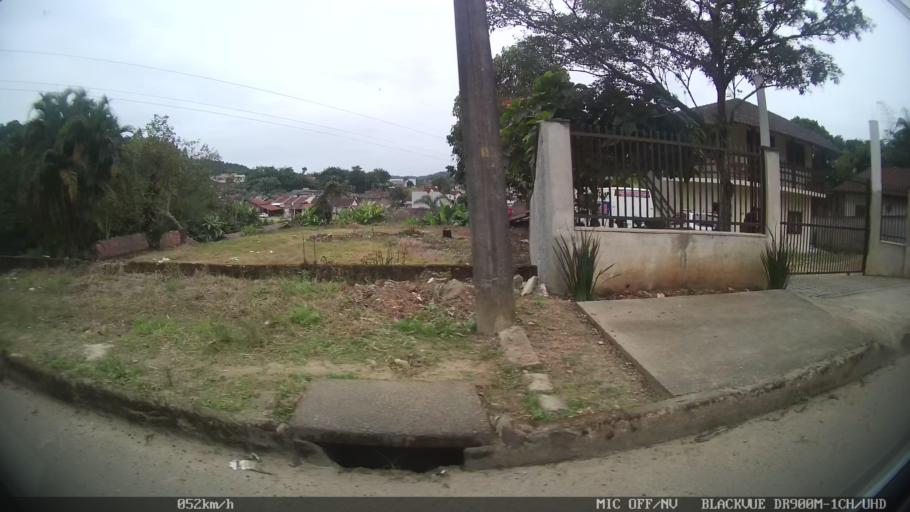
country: BR
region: Santa Catarina
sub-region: Joinville
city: Joinville
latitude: -26.3647
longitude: -48.8459
